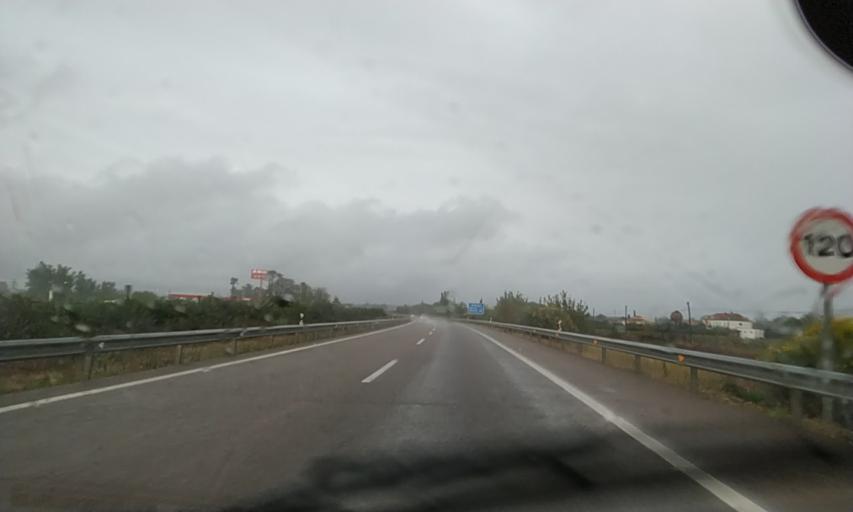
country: ES
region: Extremadura
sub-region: Provincia de Badajoz
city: Arroyo de San Servan
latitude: 38.8779
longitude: -6.4510
